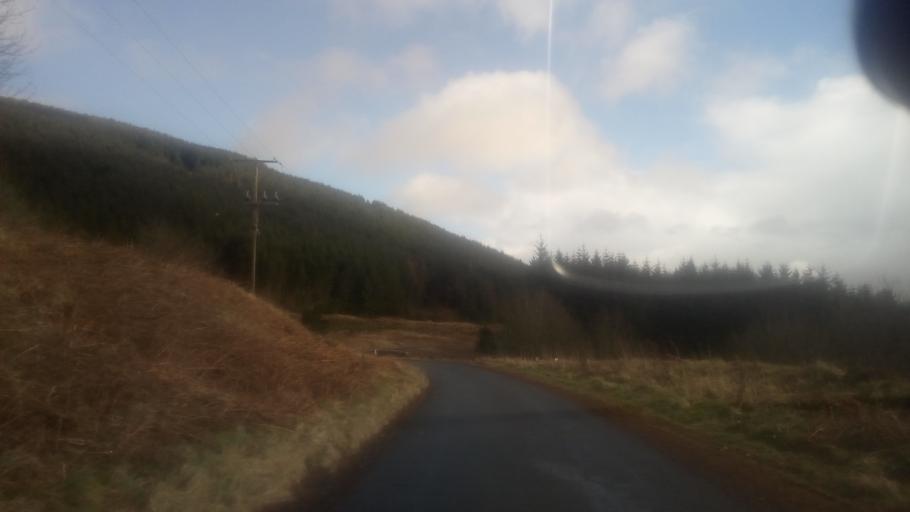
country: GB
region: Scotland
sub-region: The Scottish Borders
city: Innerleithen
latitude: 55.4686
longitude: -3.1424
